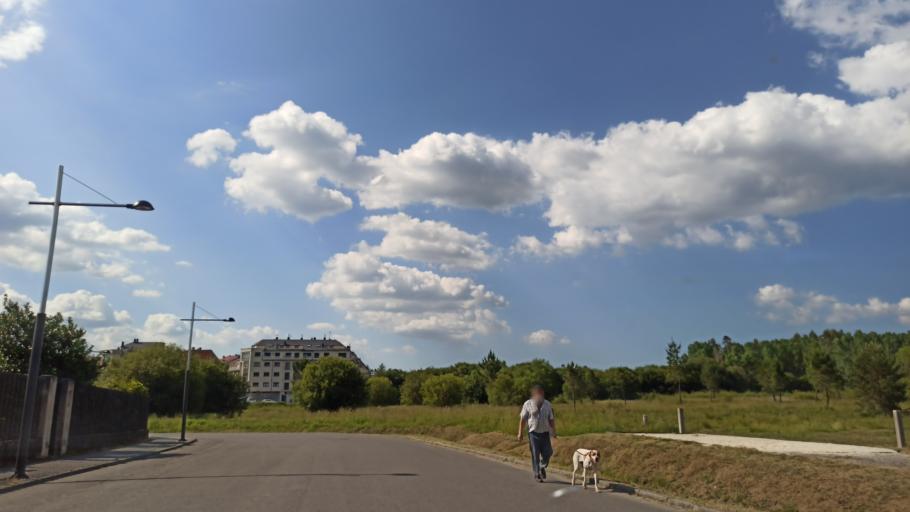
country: ES
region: Galicia
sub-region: Provincia da Coruna
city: Negreira
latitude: 42.9131
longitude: -8.7327
